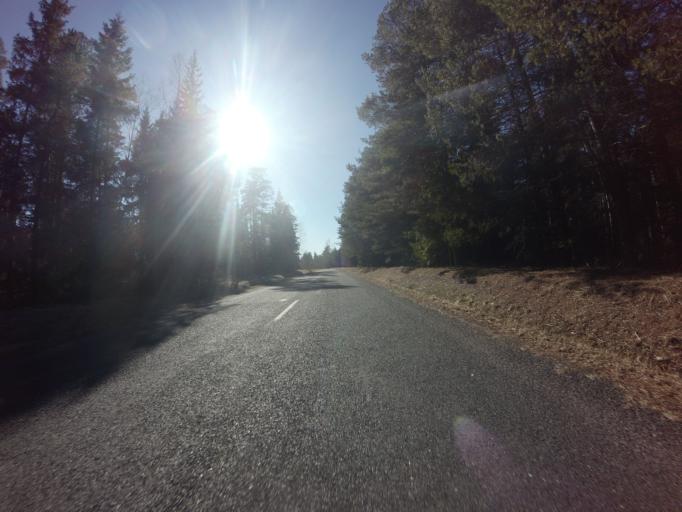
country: EE
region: Saare
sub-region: Kuressaare linn
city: Kuressaare
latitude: 58.5846
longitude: 22.5640
